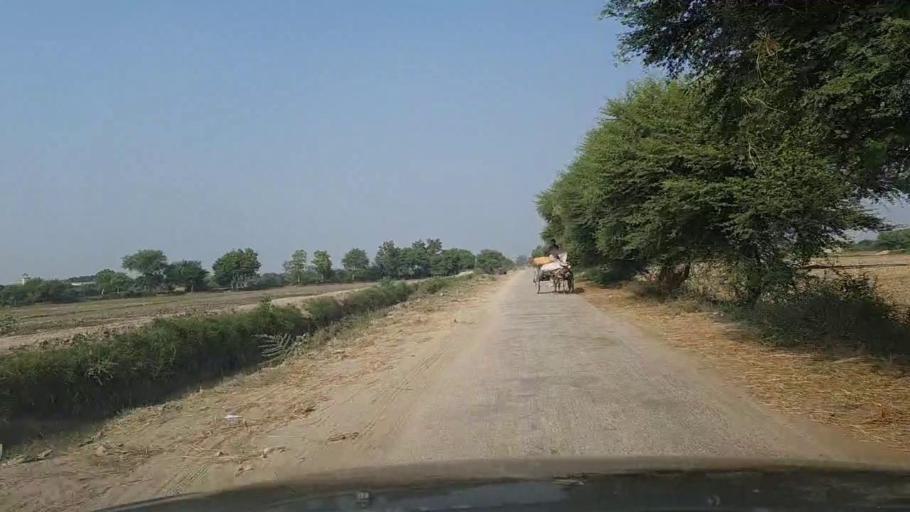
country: PK
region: Sindh
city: Mirpur Batoro
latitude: 24.7195
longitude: 68.2555
